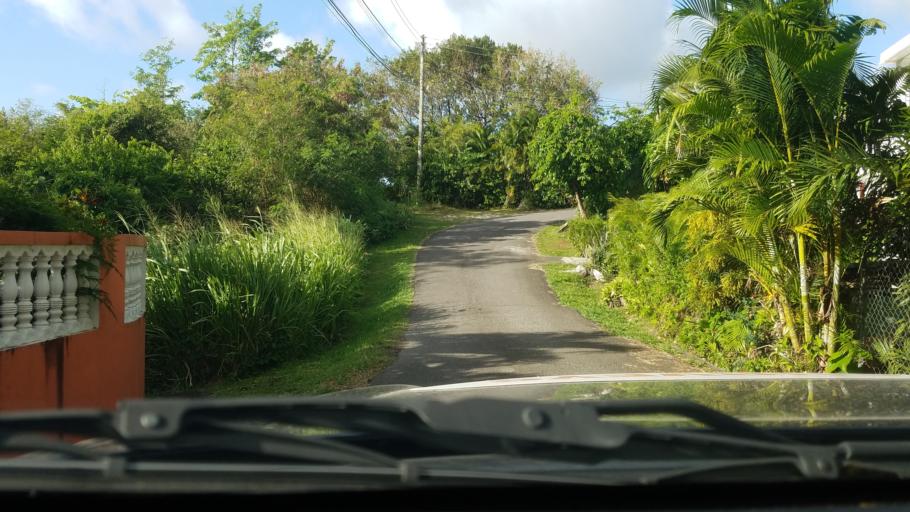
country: LC
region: Castries Quarter
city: Bisee
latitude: 14.0383
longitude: -60.9553
